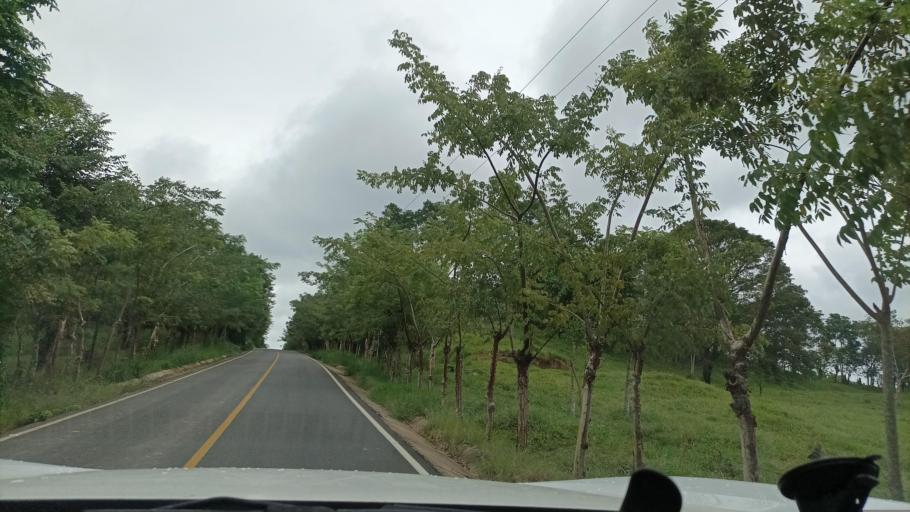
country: MX
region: Veracruz
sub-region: Moloacan
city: Cuichapa
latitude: 17.8023
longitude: -94.3573
